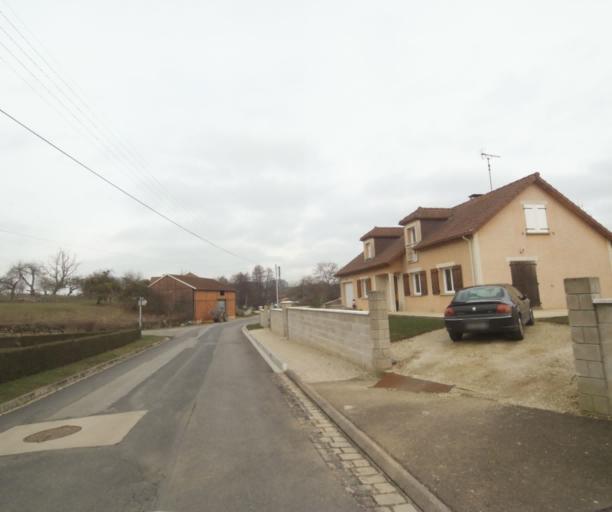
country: FR
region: Champagne-Ardenne
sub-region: Departement de la Marne
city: Sermaize-les-Bains
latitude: 48.7380
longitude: 4.9047
